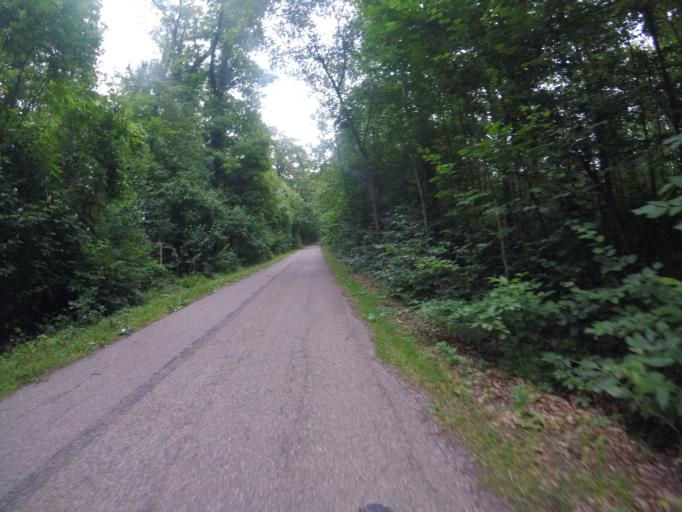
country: DE
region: Baden-Wuerttemberg
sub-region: Regierungsbezirk Stuttgart
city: Sulzbach an der Murr
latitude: 48.9828
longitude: 9.4852
